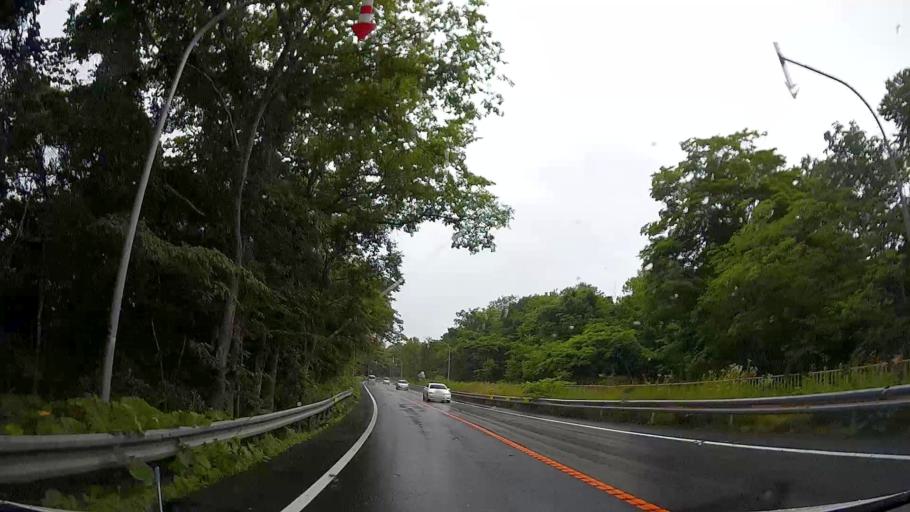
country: JP
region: Hokkaido
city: Tomakomai
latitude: 42.6845
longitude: 141.5597
